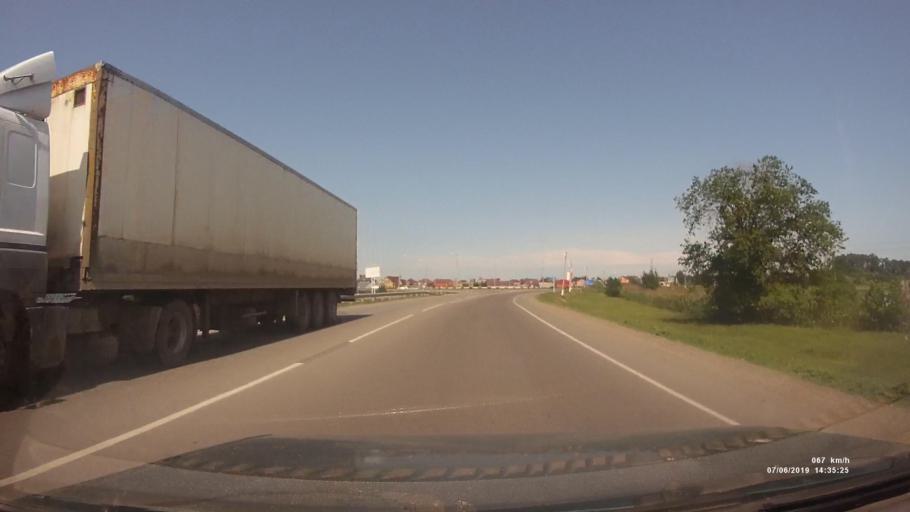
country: RU
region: Rostov
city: Bataysk
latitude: 47.1128
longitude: 39.6597
